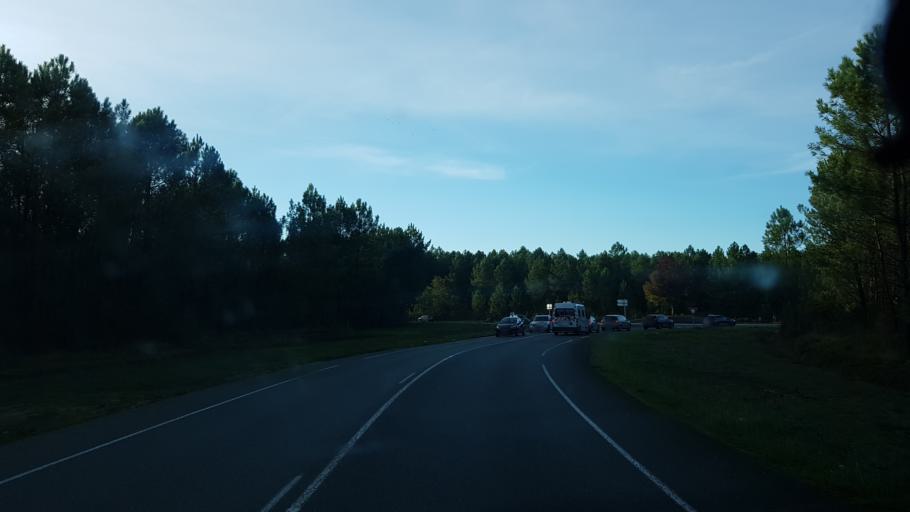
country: FR
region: Aquitaine
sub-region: Departement de la Gironde
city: Martignas-sur-Jalle
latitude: 44.8347
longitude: -0.8021
